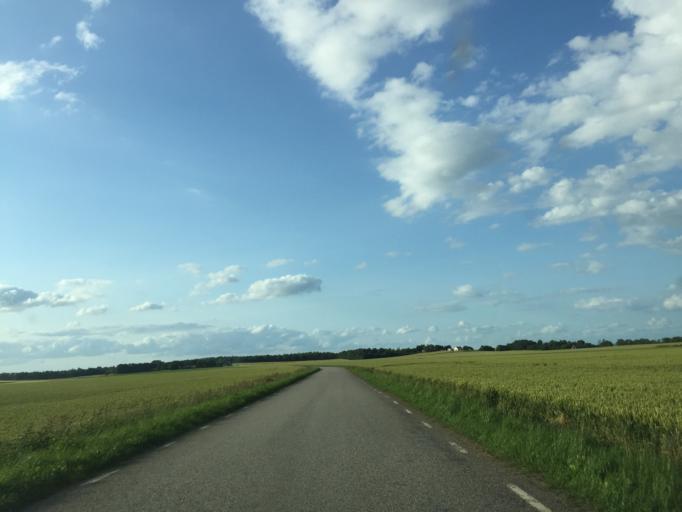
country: SE
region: OEstergoetland
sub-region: Vadstena Kommun
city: Vadstena
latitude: 58.4543
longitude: 14.8378
